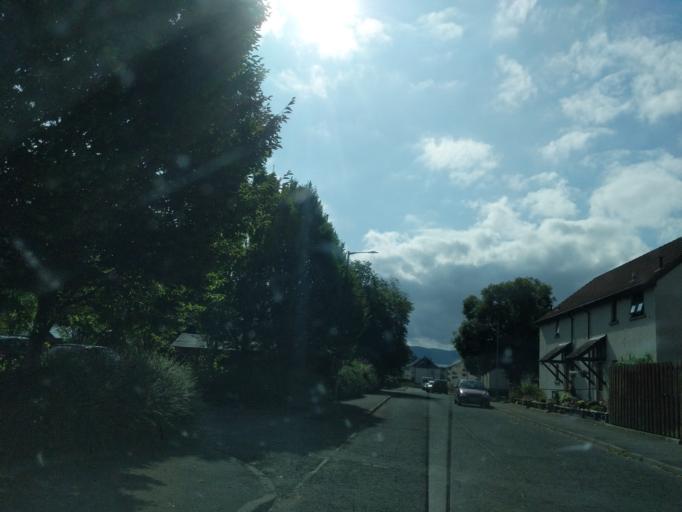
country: GB
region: Scotland
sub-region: The Scottish Borders
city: Peebles
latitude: 55.6594
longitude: -3.1960
